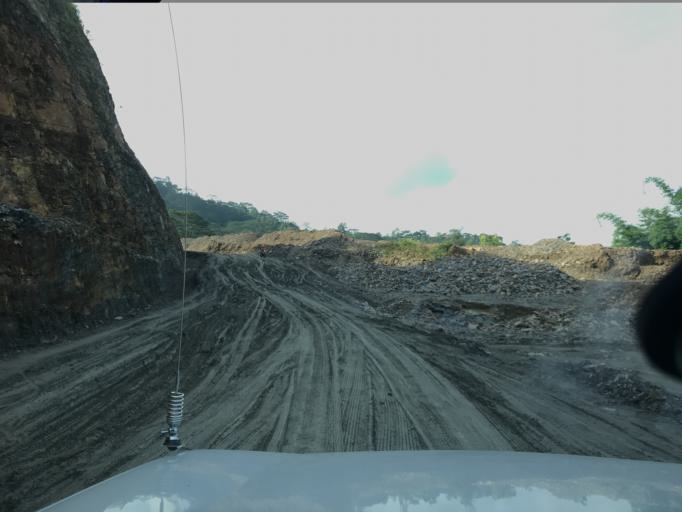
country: TL
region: Aileu
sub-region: Aileu Villa
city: Aileu
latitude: -8.6643
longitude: 125.5500
